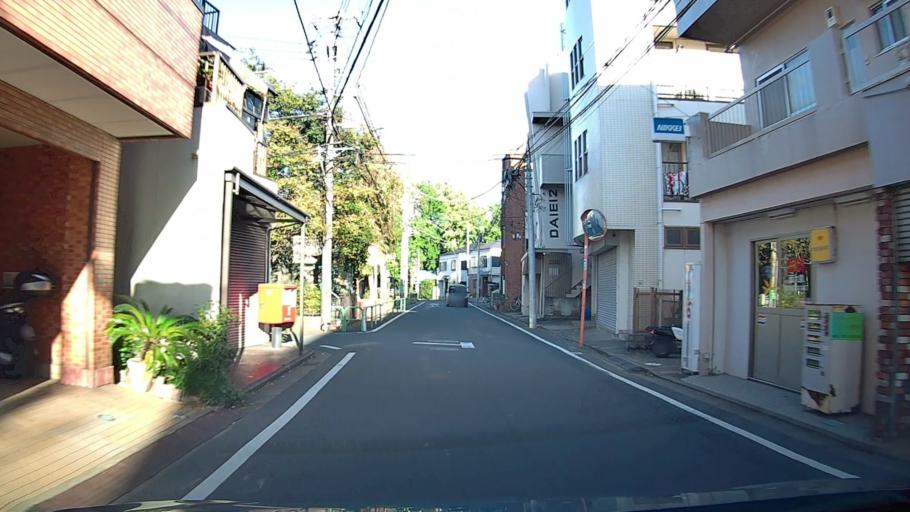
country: JP
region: Saitama
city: Wako
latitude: 35.7542
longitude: 139.5839
